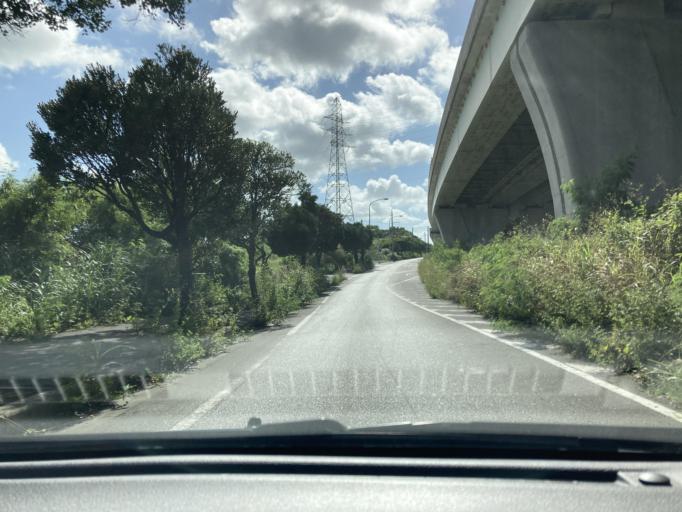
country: JP
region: Okinawa
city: Tomigusuku
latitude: 26.1828
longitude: 127.7326
